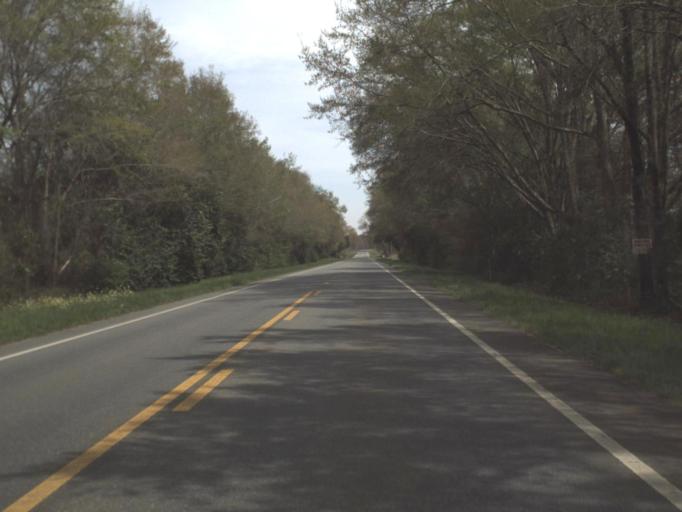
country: US
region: Alabama
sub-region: Houston County
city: Cottonwood
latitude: 30.9473
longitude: -85.3774
